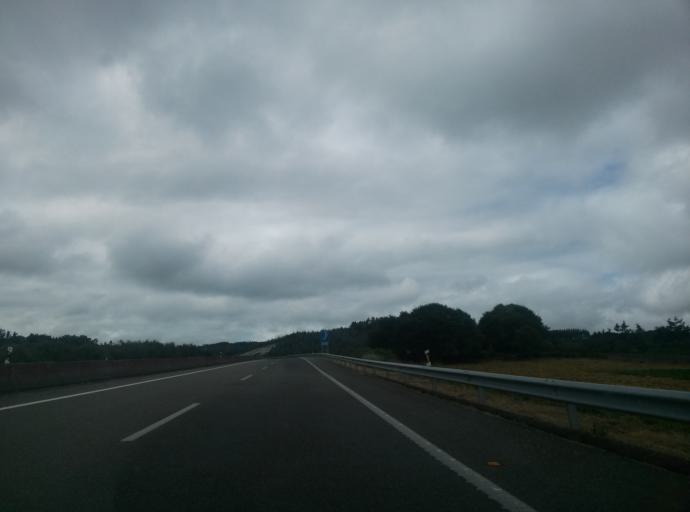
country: ES
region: Galicia
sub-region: Provincia de Lugo
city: Vilalba
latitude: 43.3372
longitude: -7.7045
